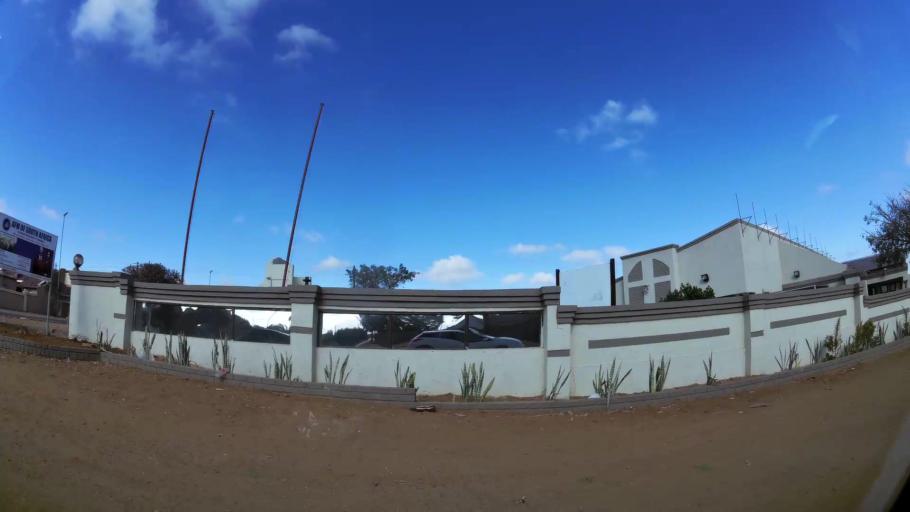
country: ZA
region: Limpopo
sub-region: Capricorn District Municipality
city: Polokwane
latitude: -23.8573
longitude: 29.3757
